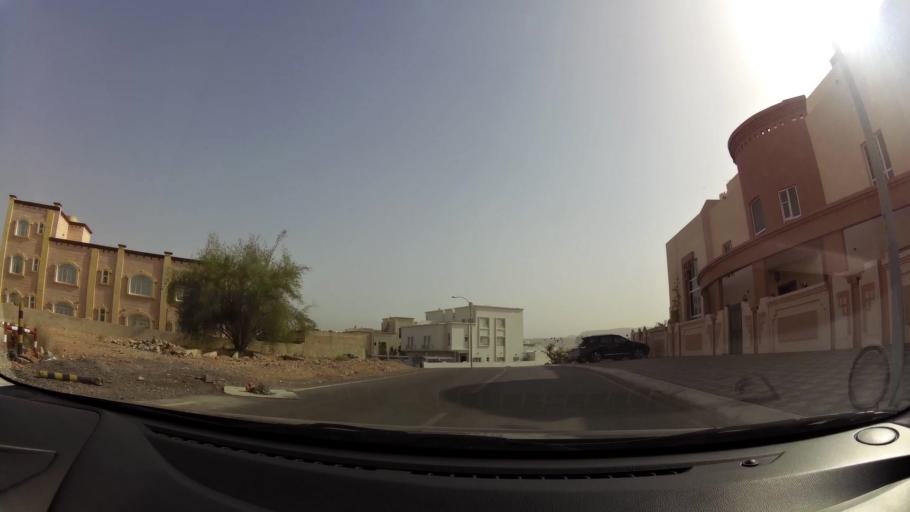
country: OM
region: Muhafazat Masqat
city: Bawshar
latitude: 23.5571
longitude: 58.3534
